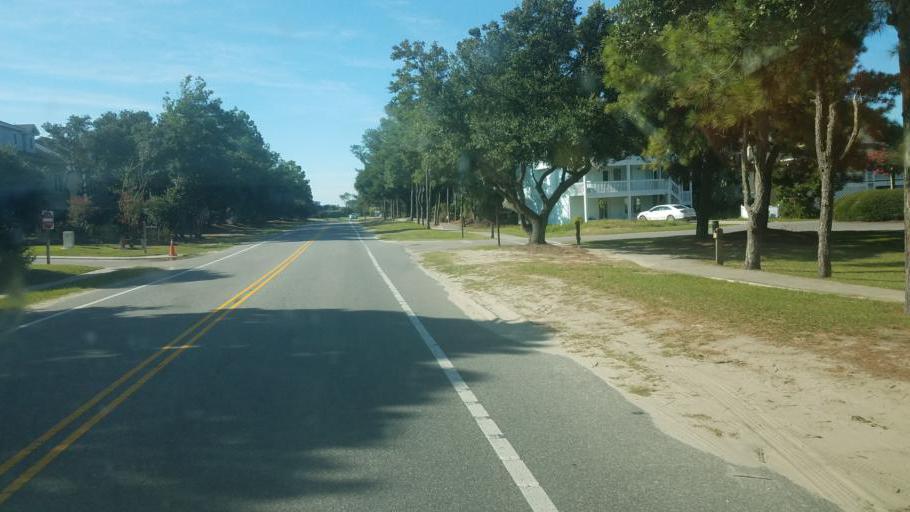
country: US
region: North Carolina
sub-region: Currituck County
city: Currituck
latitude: 36.3682
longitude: -75.8276
